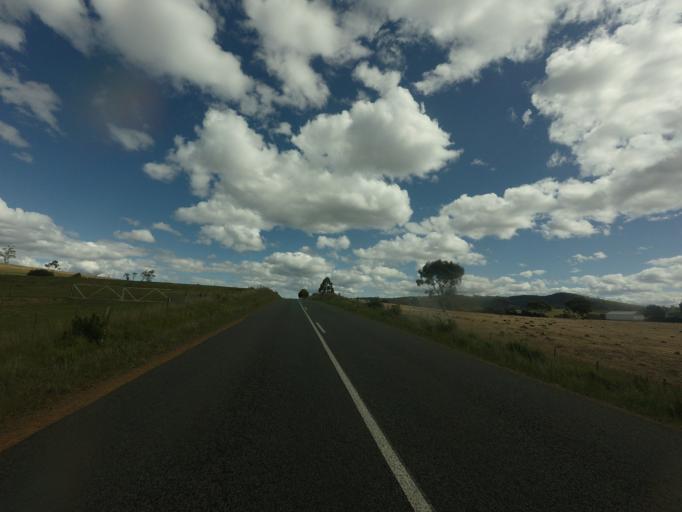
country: AU
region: Tasmania
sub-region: Brighton
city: Bridgewater
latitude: -42.3909
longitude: 147.3149
